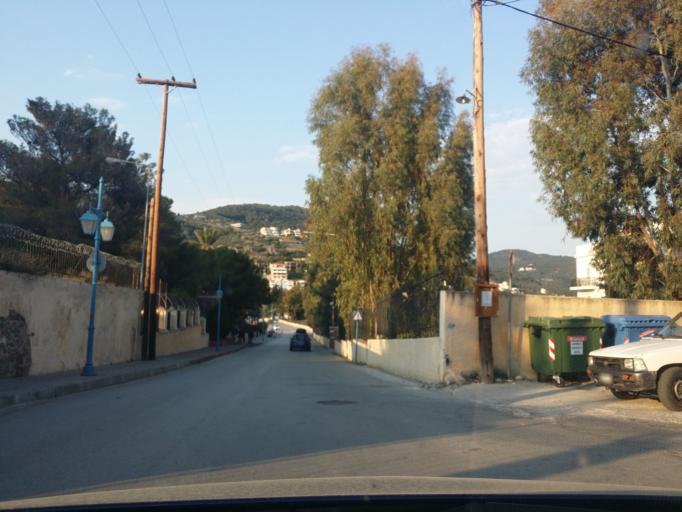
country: GR
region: Attica
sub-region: Nomos Piraios
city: Poros
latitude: 37.5055
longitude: 23.4576
